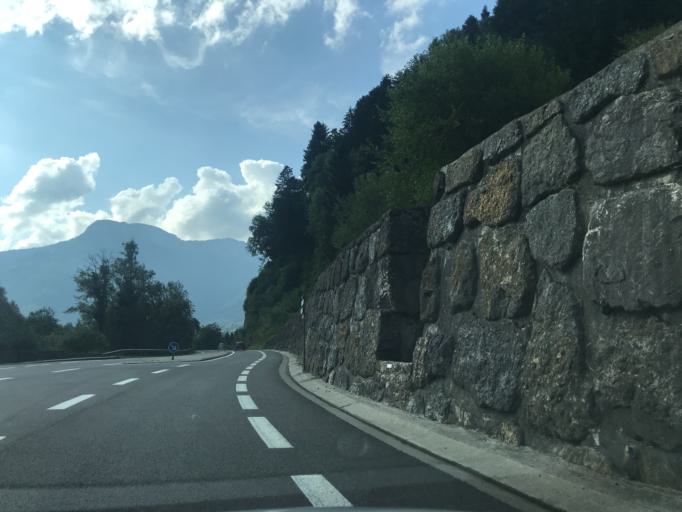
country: FR
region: Rhone-Alpes
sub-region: Departement de la Haute-Savoie
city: Dingy-Saint-Clair
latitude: 45.9035
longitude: 6.2094
